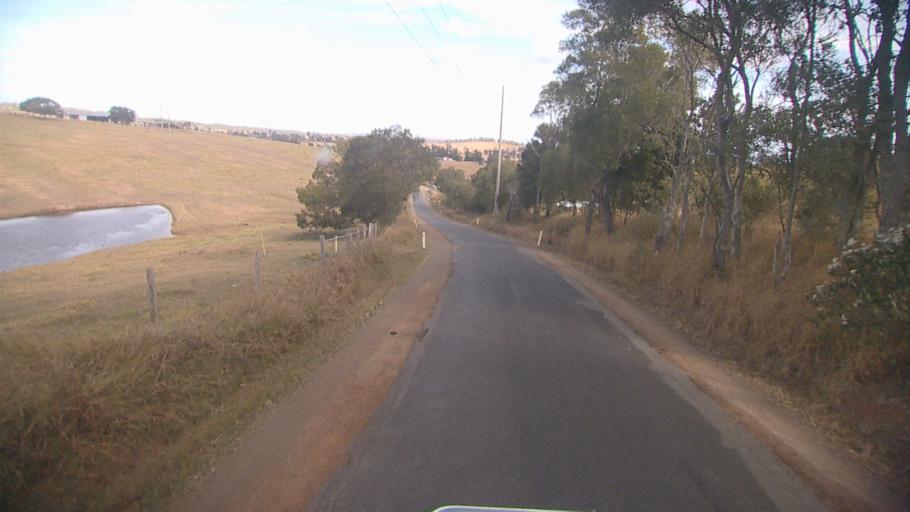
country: AU
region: Queensland
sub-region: Logan
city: Cedar Vale
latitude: -27.9062
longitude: 153.0138
